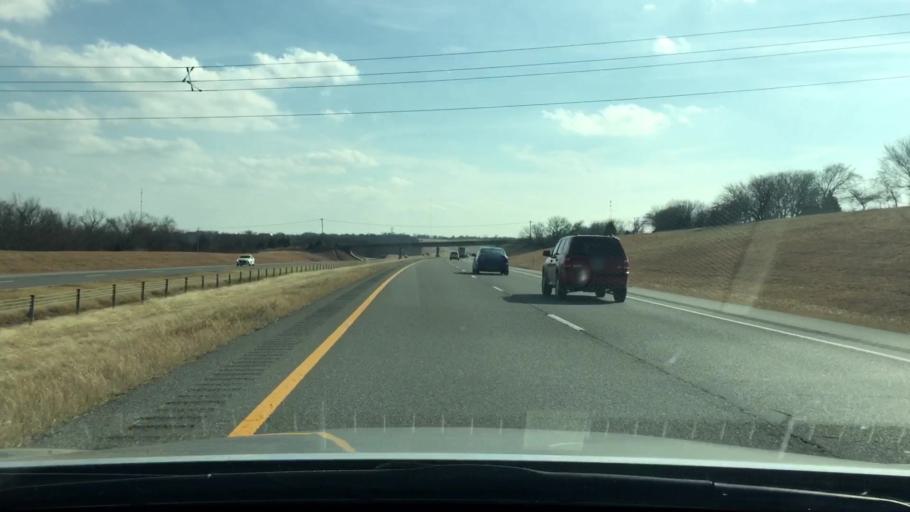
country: US
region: Oklahoma
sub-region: McClain County
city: Purcell
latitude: 34.9607
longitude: -97.3694
